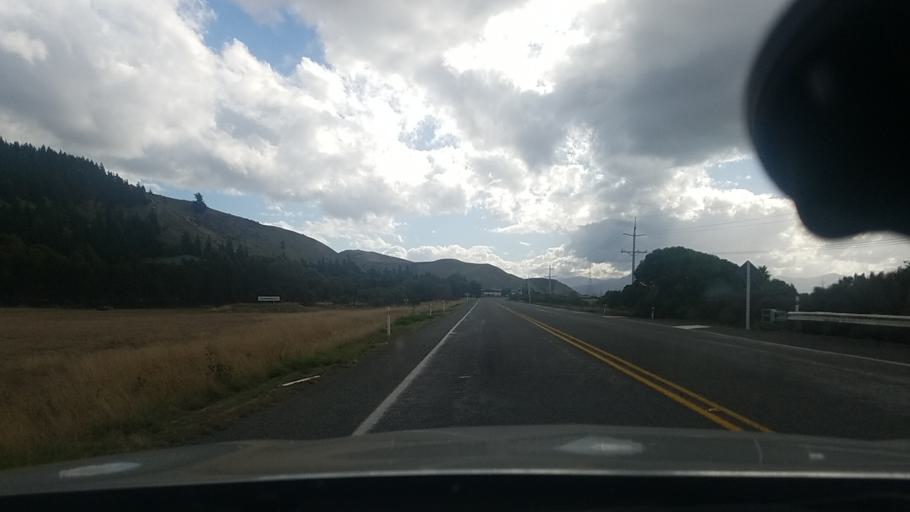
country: NZ
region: Marlborough
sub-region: Marlborough District
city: Blenheim
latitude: -41.5440
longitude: 174.0389
